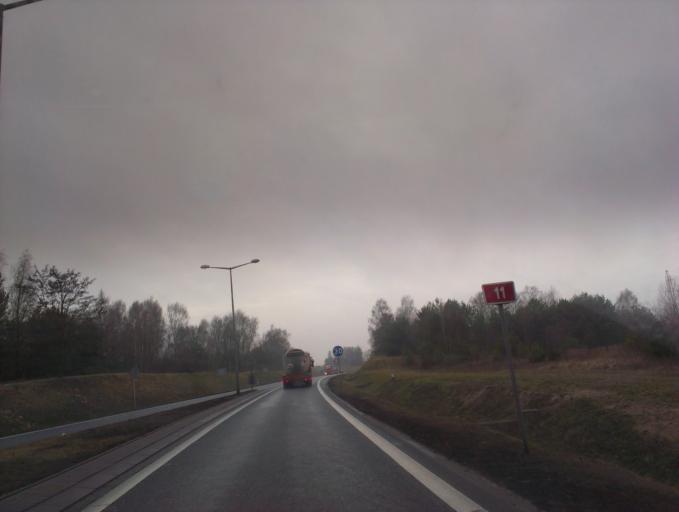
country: PL
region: Greater Poland Voivodeship
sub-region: Powiat pilski
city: Pila
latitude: 53.1487
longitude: 16.7881
